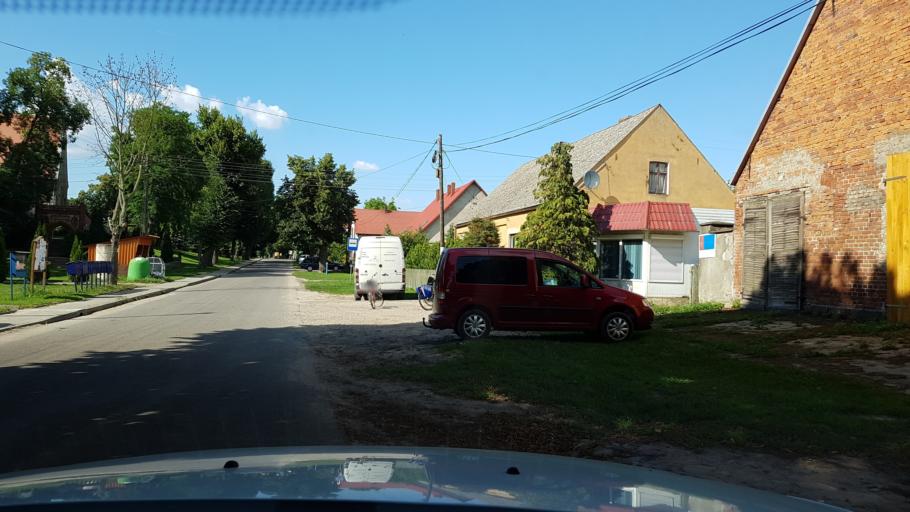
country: PL
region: West Pomeranian Voivodeship
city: Trzcinsko Zdroj
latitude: 52.9522
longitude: 14.5491
